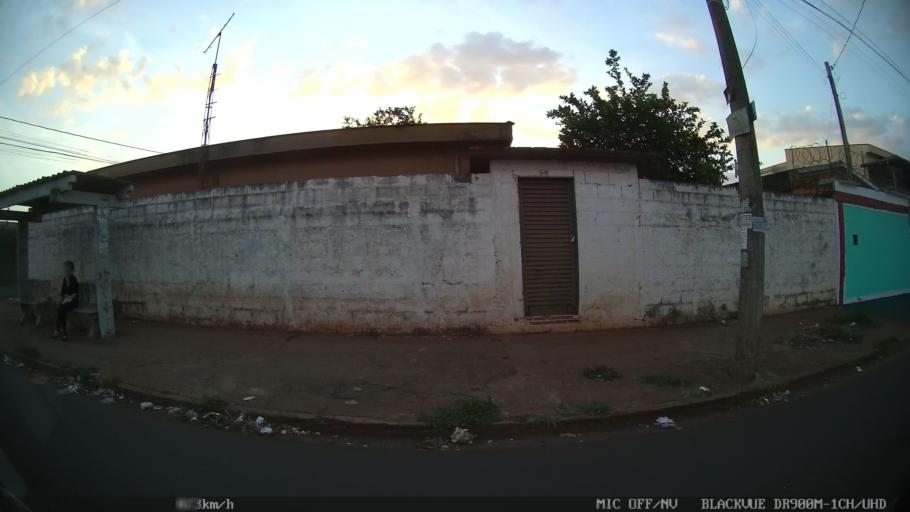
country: BR
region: Sao Paulo
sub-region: Ribeirao Preto
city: Ribeirao Preto
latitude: -21.1447
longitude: -47.8212
